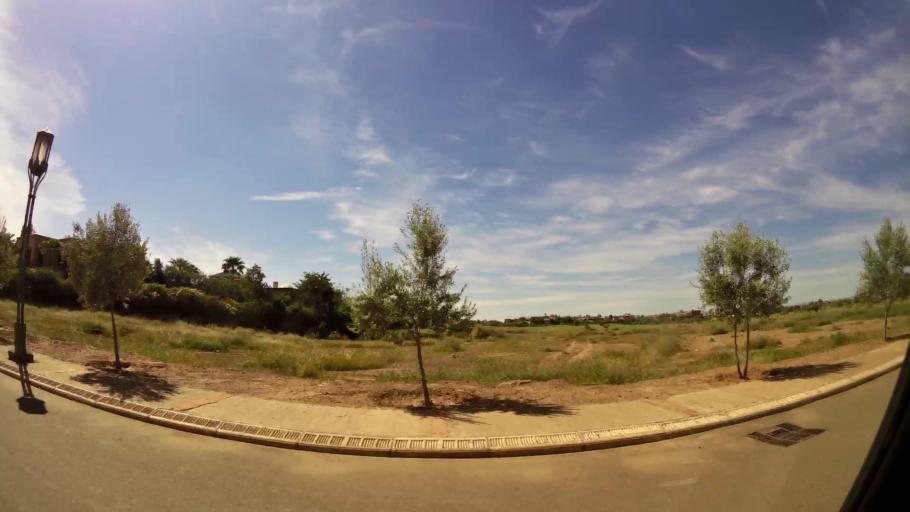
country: MA
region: Marrakech-Tensift-Al Haouz
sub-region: Marrakech
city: Marrakesh
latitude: 31.6137
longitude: -7.9297
